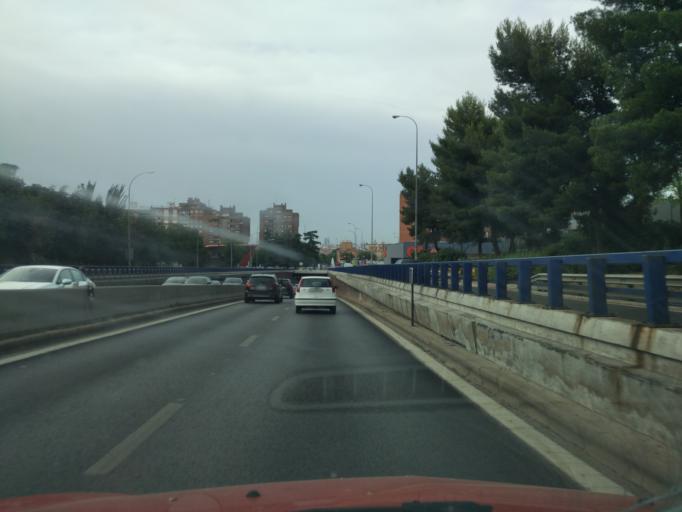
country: ES
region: Madrid
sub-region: Provincia de Madrid
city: Carabanchel
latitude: 40.3826
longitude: -3.7183
